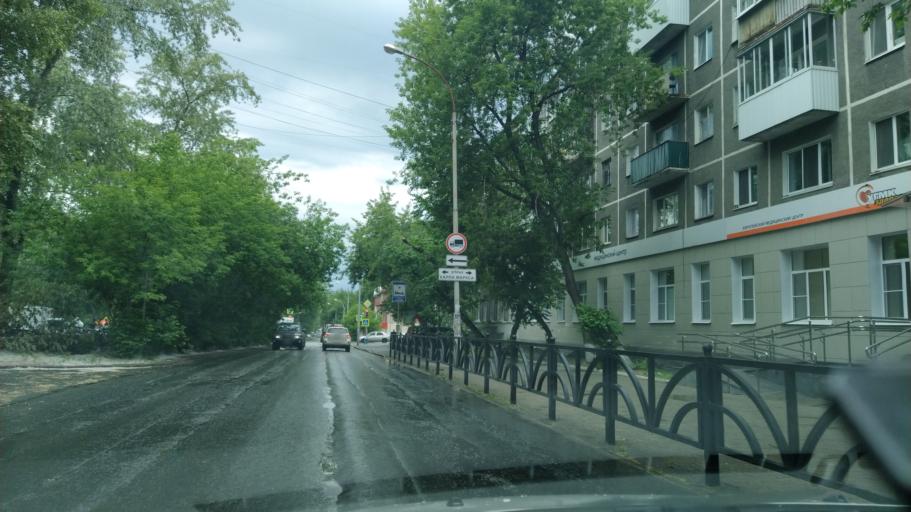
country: RU
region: Sverdlovsk
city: Yekaterinburg
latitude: 56.8315
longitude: 60.6294
